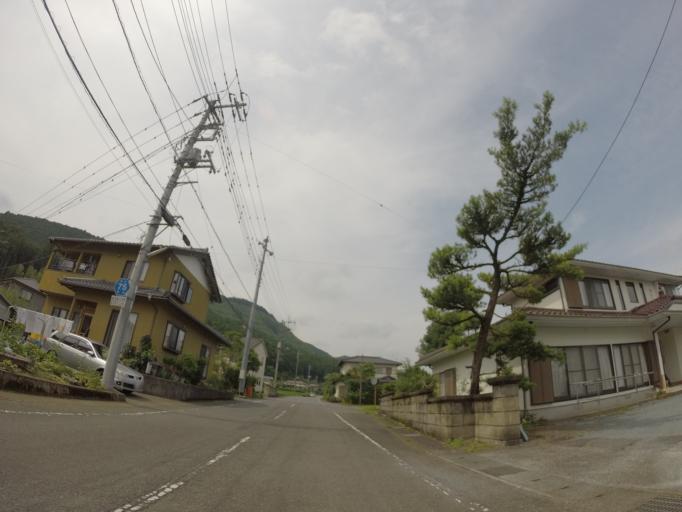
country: JP
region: Shizuoka
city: Fujinomiya
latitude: 35.2714
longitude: 138.5599
